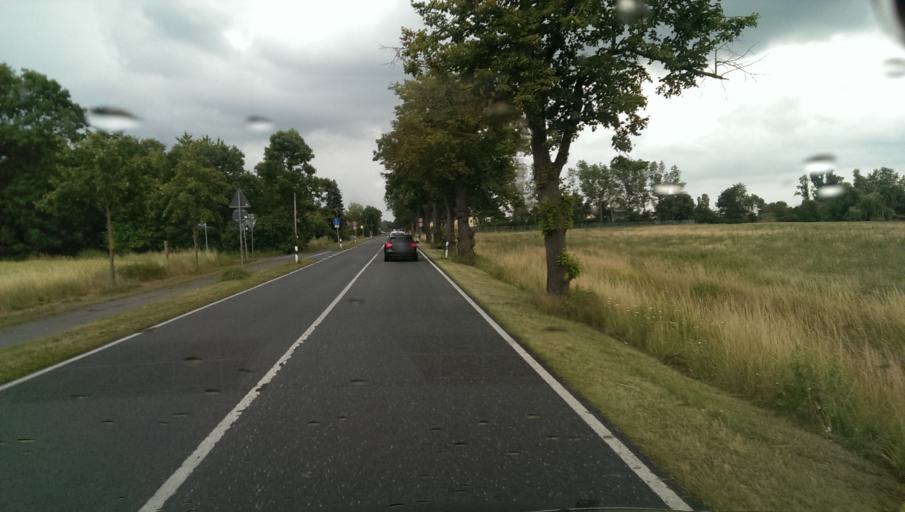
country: DE
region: Brandenburg
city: Rathenow
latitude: 52.6306
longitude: 12.3320
